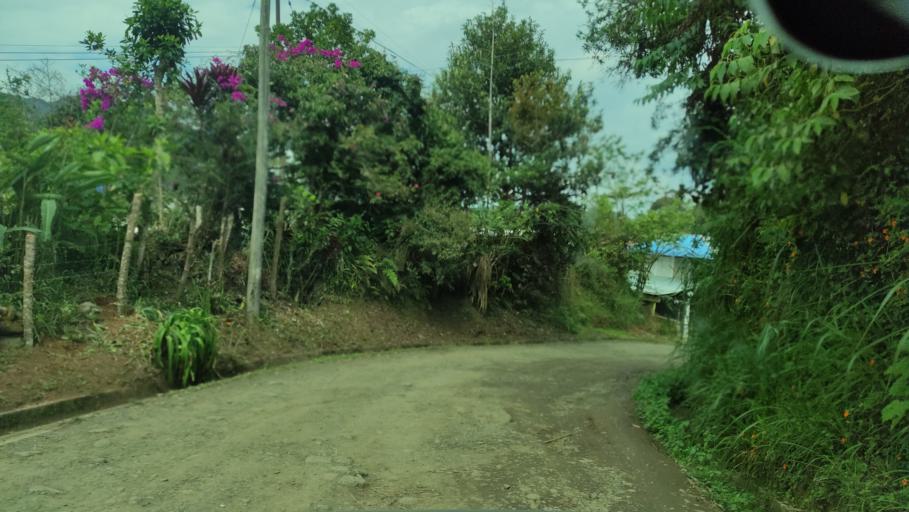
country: CO
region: Valle del Cauca
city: Cali
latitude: 3.4534
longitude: -76.6355
